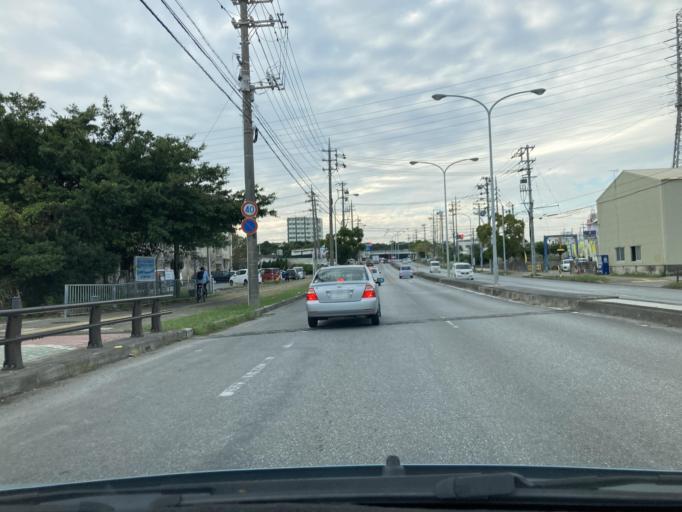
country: JP
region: Okinawa
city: Okinawa
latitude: 26.3536
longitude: 127.8078
